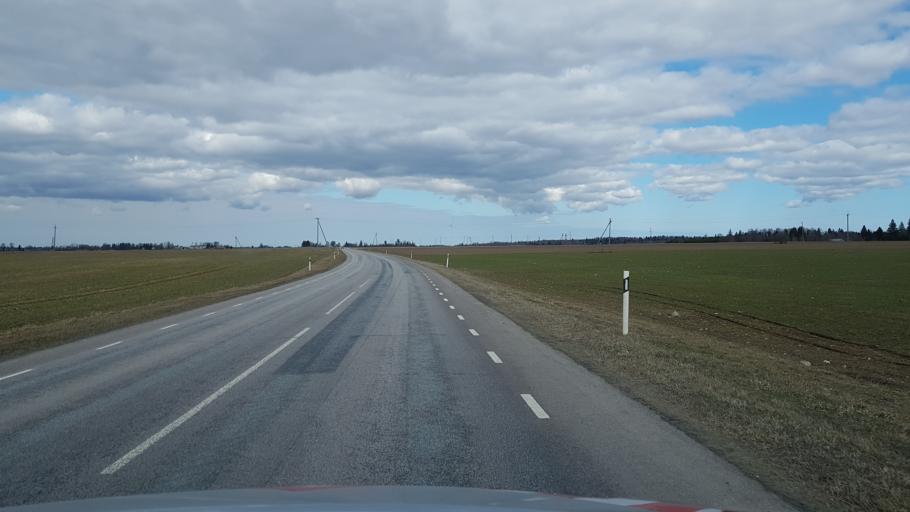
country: EE
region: Laeaene-Virumaa
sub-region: Vaeike-Maarja vald
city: Vaike-Maarja
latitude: 59.1625
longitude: 26.2662
